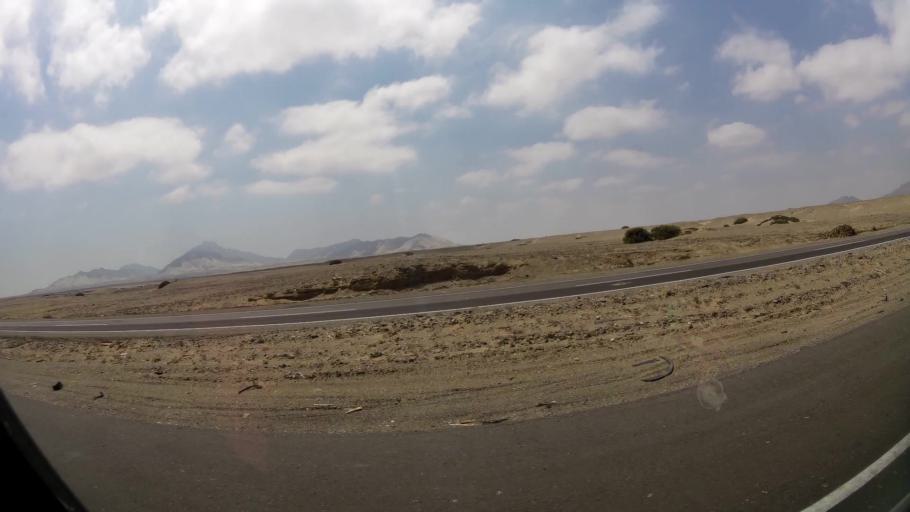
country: PE
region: La Libertad
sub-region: Ascope
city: Paijan
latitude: -7.6494
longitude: -79.3468
